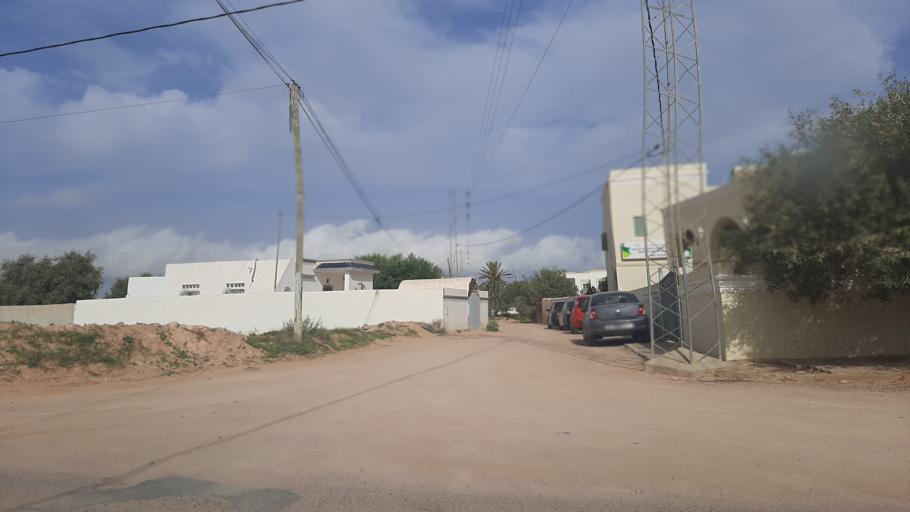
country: TN
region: Madanin
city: Midoun
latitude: 33.7981
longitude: 11.0287
